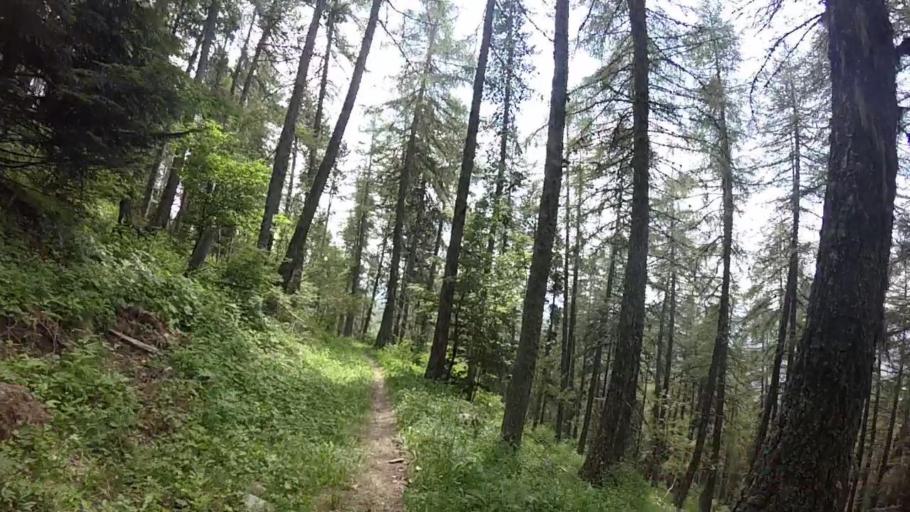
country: FR
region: Provence-Alpes-Cote d'Azur
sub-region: Departement des Alpes-de-Haute-Provence
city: Seyne-les-Alpes
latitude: 44.4092
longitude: 6.3718
